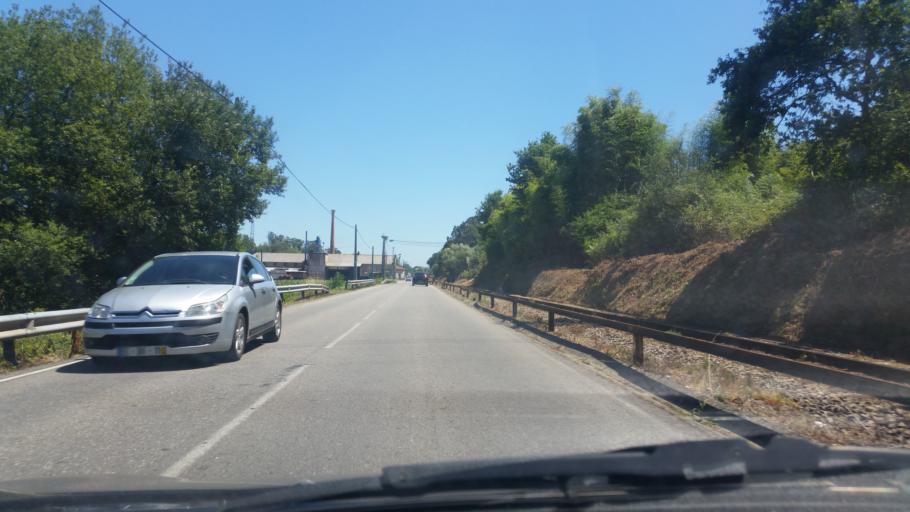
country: PT
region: Aveiro
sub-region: Aveiro
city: Eixo
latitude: 40.6150
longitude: -8.5371
